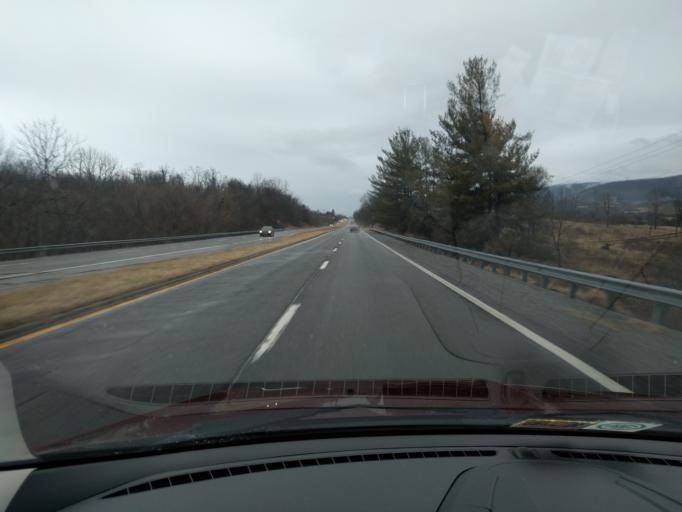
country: US
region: Virginia
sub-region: Giles County
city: Pembroke
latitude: 37.3059
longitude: -80.5734
